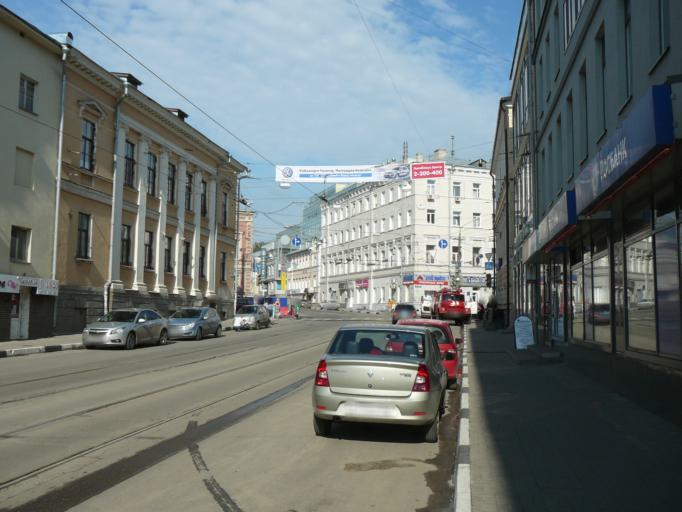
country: RU
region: Nizjnij Novgorod
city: Nizhniy Novgorod
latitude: 56.3243
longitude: 44.0078
